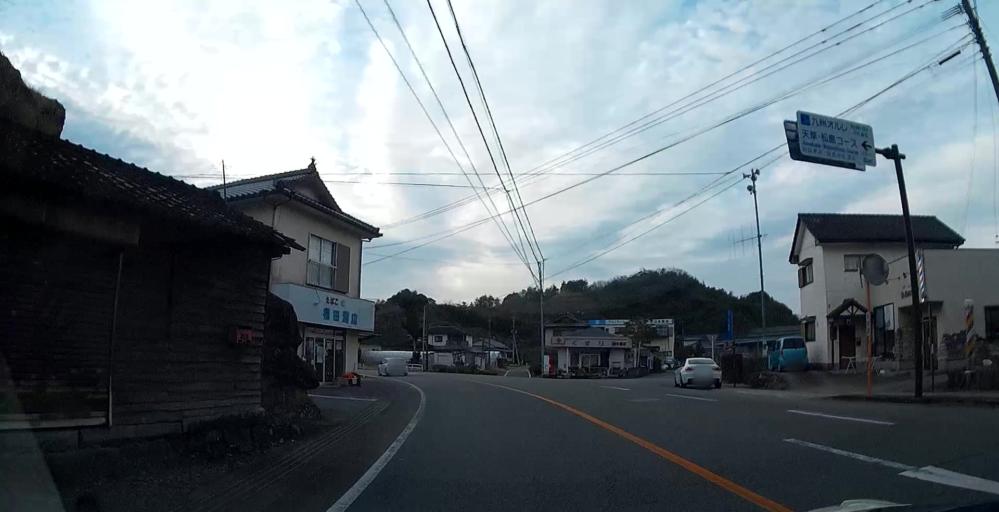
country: JP
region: Kumamoto
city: Yatsushiro
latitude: 32.5004
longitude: 130.4016
